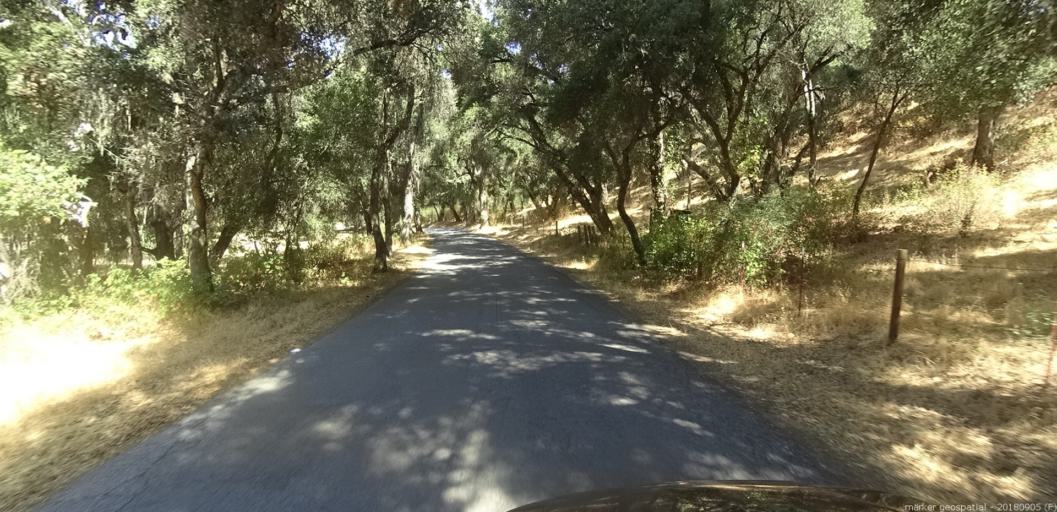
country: US
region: California
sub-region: Monterey County
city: Carmel Valley Village
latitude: 36.4005
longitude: -121.6563
